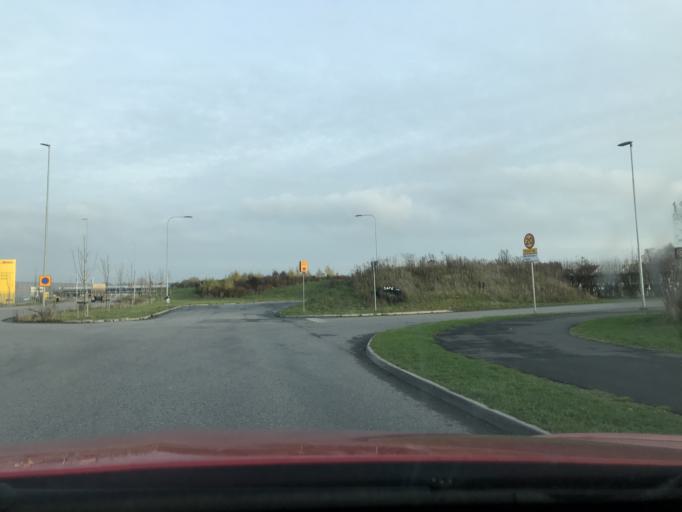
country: SE
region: Skane
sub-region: Burlovs Kommun
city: Arloev
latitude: 55.6070
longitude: 13.1004
